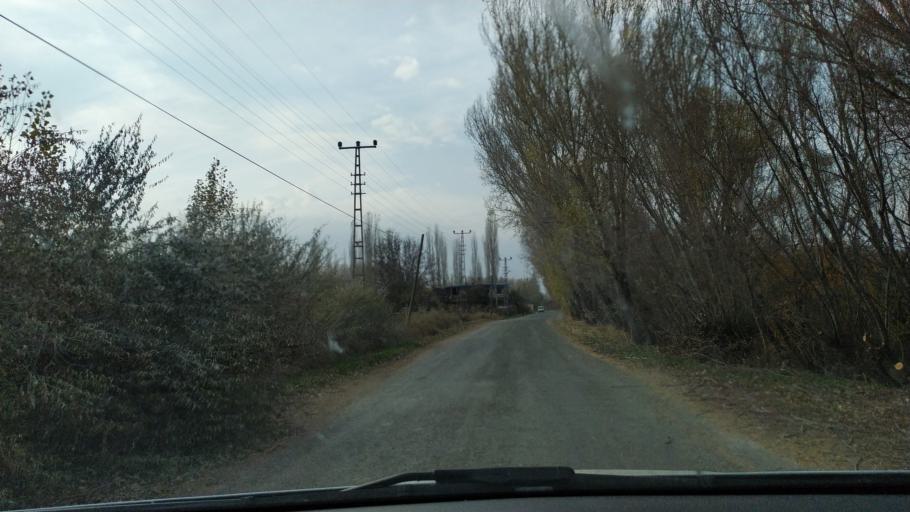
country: TR
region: Kayseri
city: Akkisla
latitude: 38.9954
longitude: 36.1184
